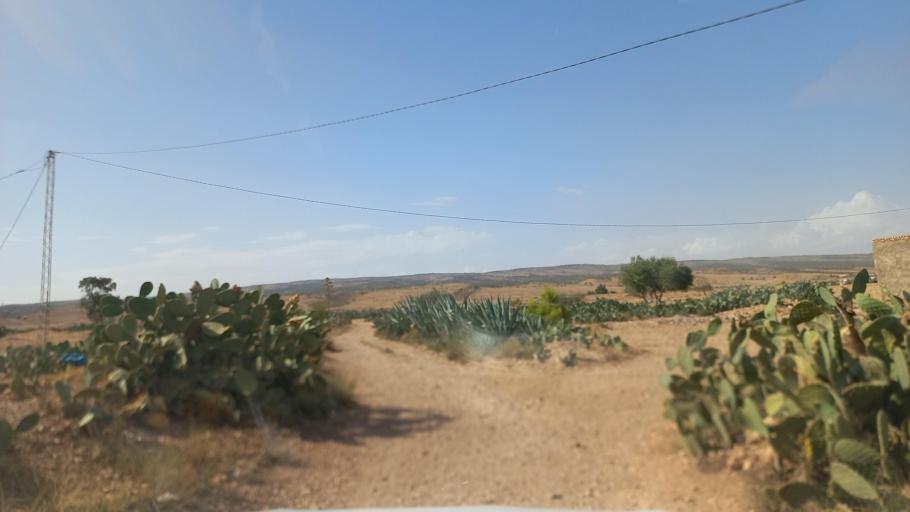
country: TN
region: Al Qasrayn
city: Kasserine
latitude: 35.2865
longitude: 8.9382
